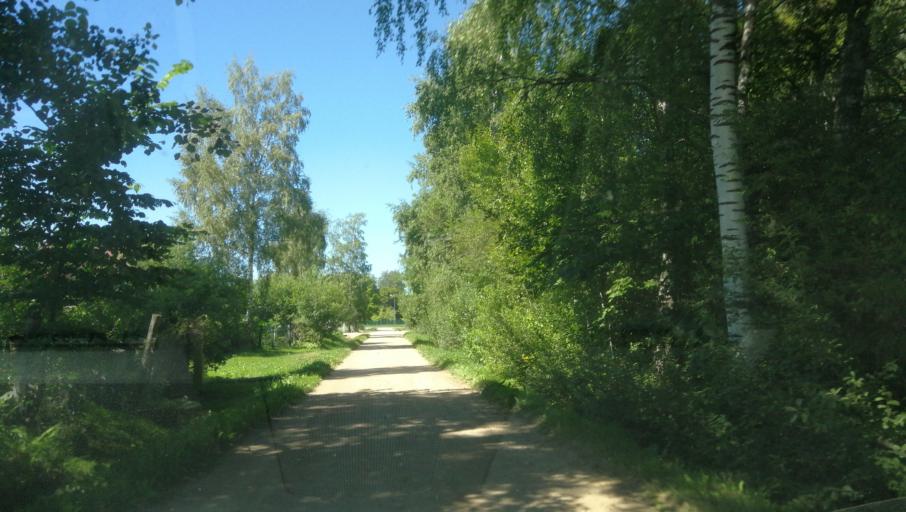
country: LV
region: Cesu Rajons
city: Cesis
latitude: 57.3049
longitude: 25.2910
